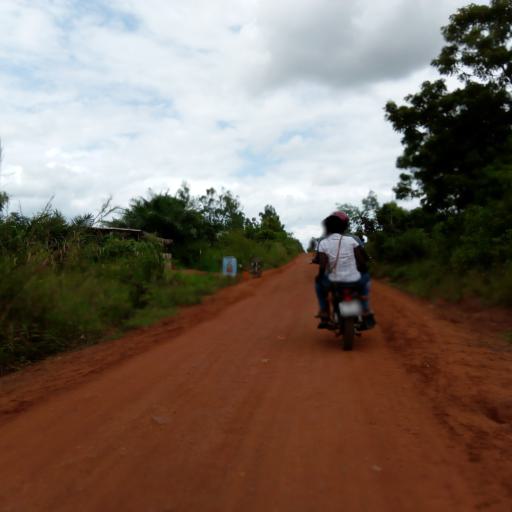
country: TG
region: Maritime
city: Tsevie
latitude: 6.3377
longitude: 1.0943
